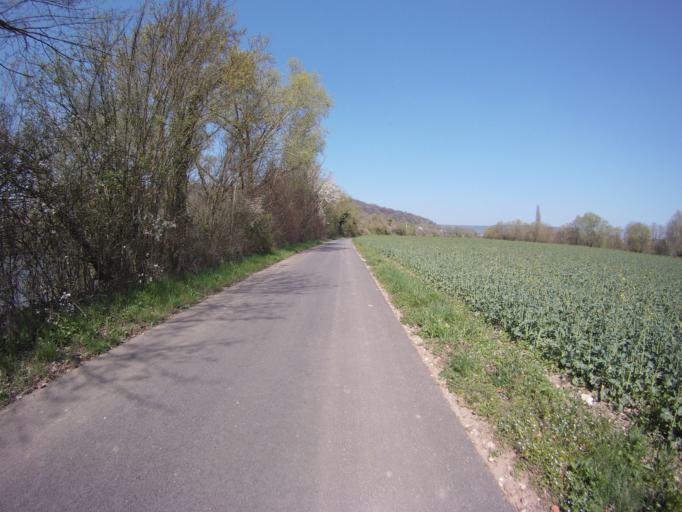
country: FR
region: Lorraine
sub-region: Departement de Meurthe-et-Moselle
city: Marbache
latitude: 48.7975
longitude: 6.1110
